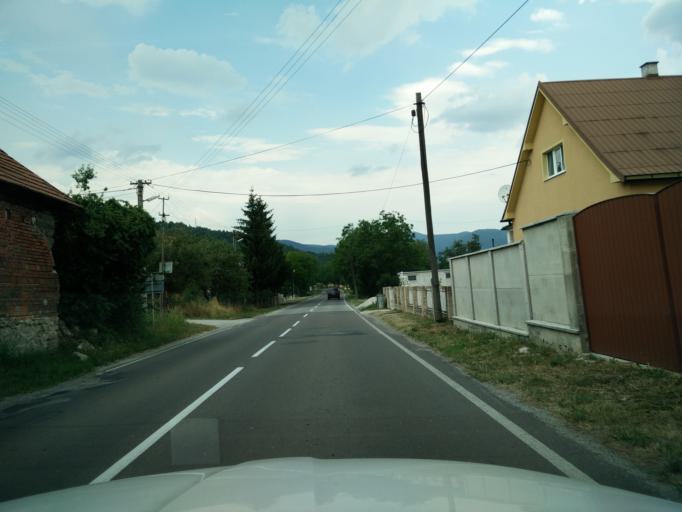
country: SK
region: Nitriansky
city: Novaky
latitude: 48.7781
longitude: 18.4884
